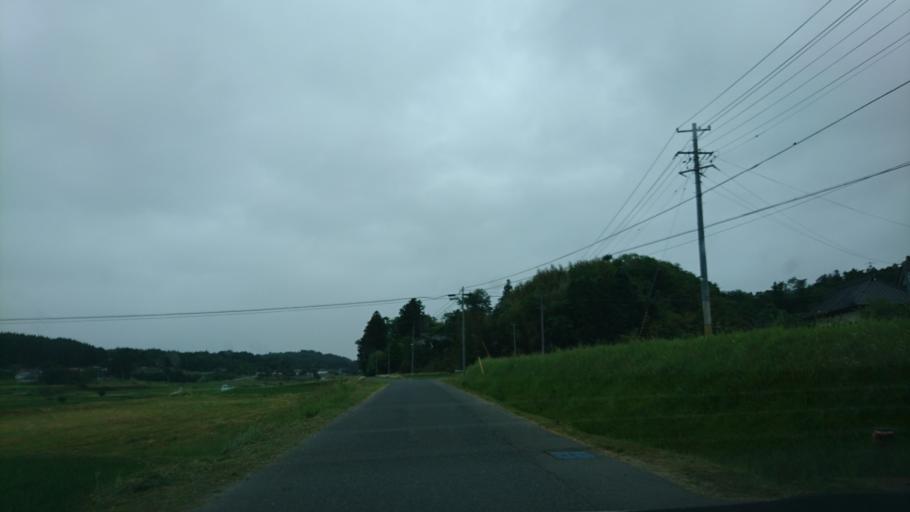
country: JP
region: Iwate
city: Ichinoseki
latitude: 38.9164
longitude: 141.1789
